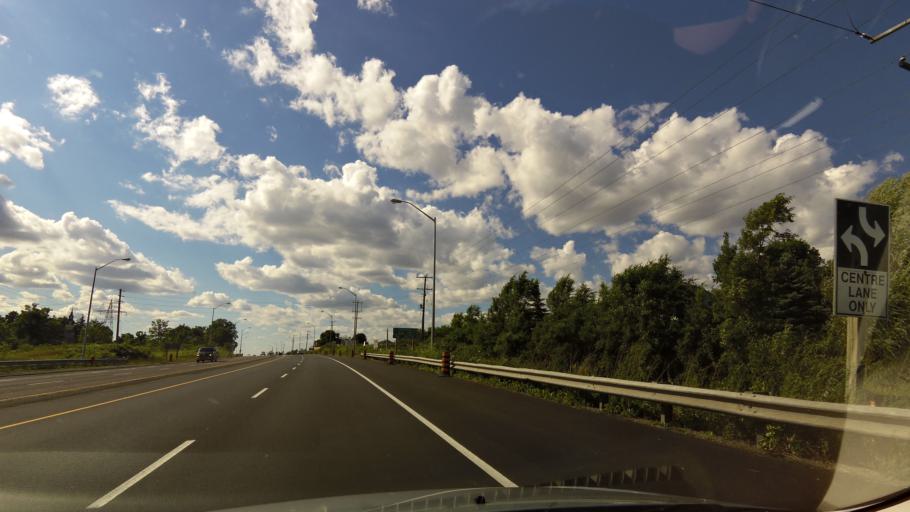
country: CA
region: Ontario
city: Ancaster
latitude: 43.3977
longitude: -80.0325
